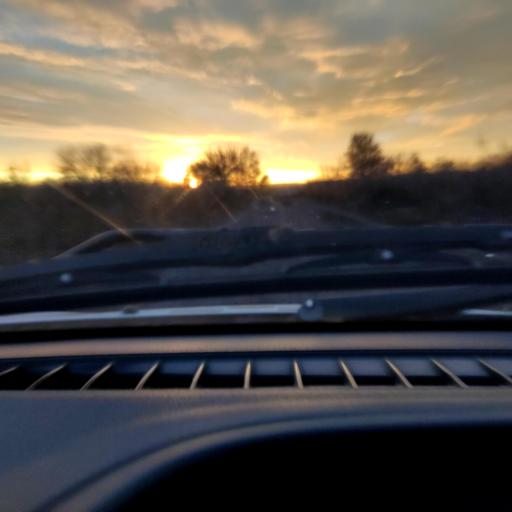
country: RU
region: Samara
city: Tol'yatti
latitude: 53.5948
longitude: 49.4849
